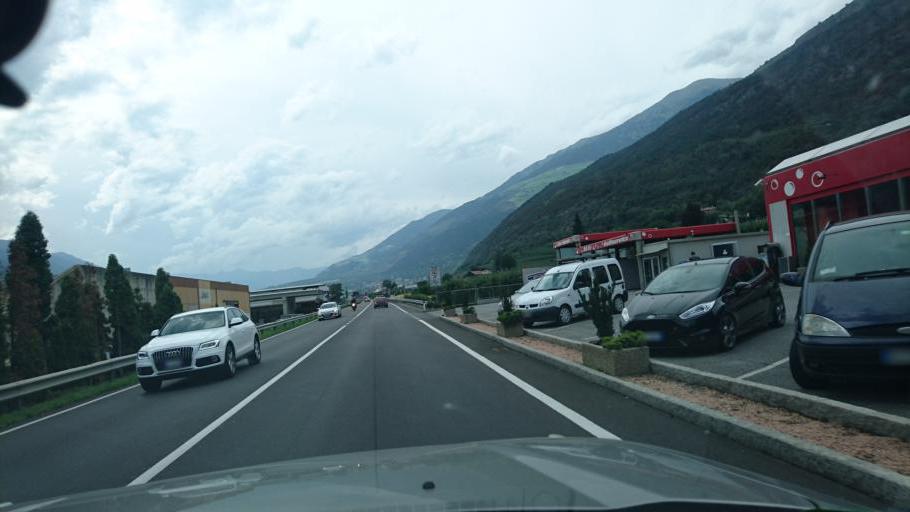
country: IT
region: Trentino-Alto Adige
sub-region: Bolzano
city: Silandro
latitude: 46.6225
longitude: 10.8112
